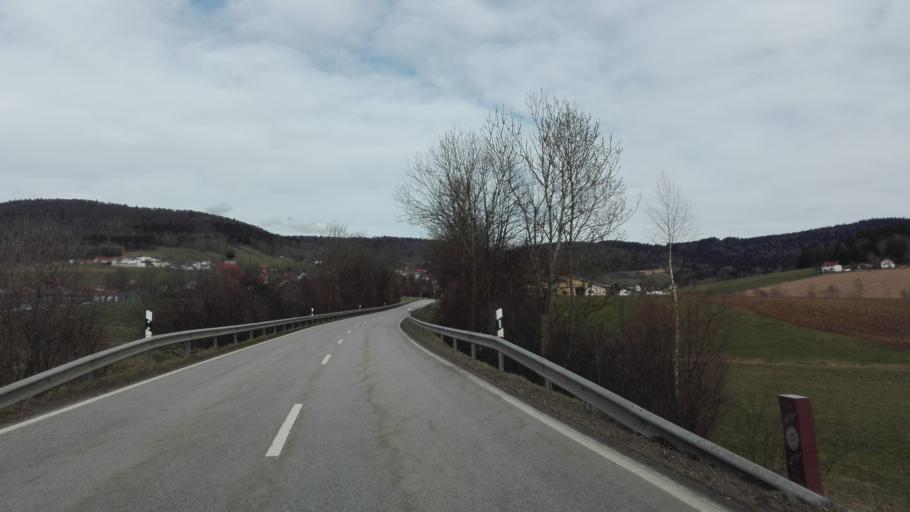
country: DE
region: Bavaria
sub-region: Lower Bavaria
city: Hauzenberg
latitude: 48.6317
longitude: 13.6594
